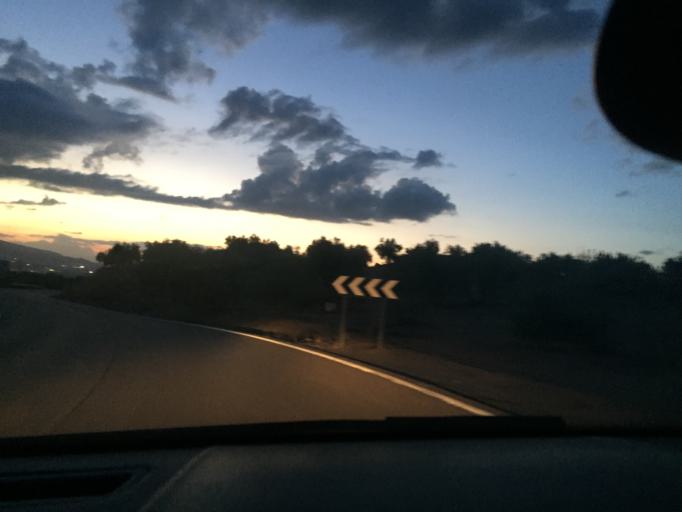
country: ES
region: Andalusia
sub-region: Provincia de Jaen
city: Mancha Real
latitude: 37.7987
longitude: -3.6512
